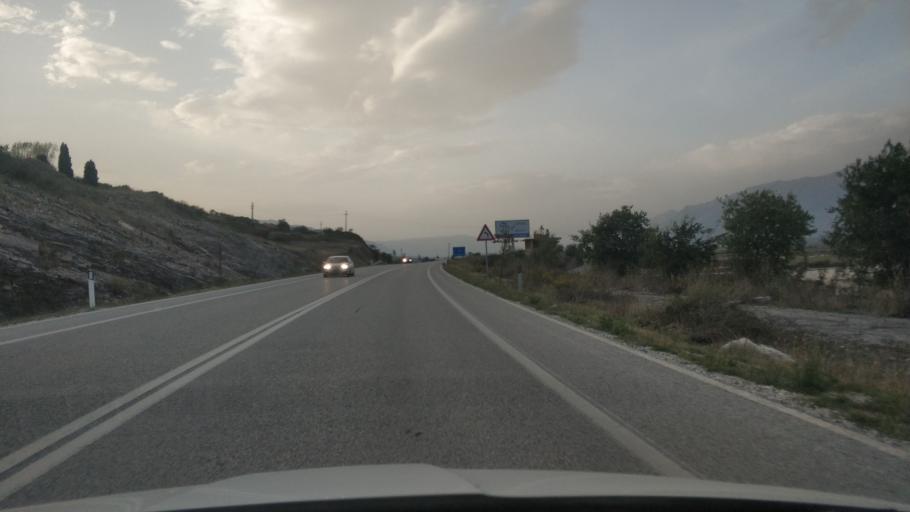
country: AL
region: Gjirokaster
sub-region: Rrethi i Gjirokastres
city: Libohove
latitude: 39.9476
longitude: 20.2588
